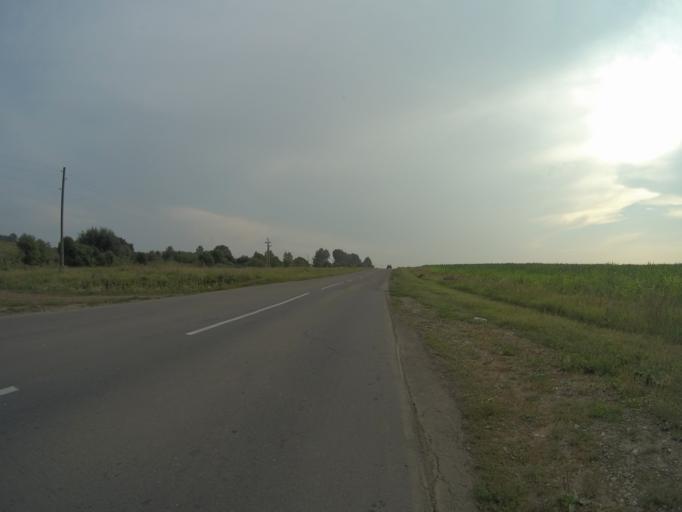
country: RU
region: Ivanovo
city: Gavrilov Posad
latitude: 56.3480
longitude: 40.2075
